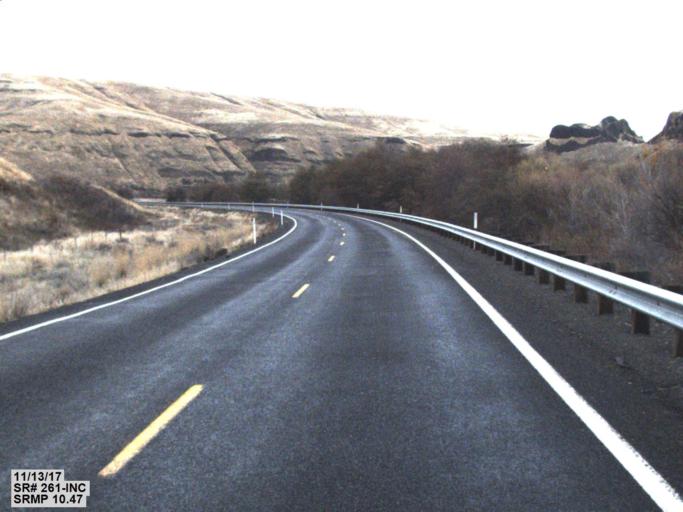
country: US
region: Washington
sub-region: Walla Walla County
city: Waitsburg
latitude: 46.5439
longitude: -118.1642
